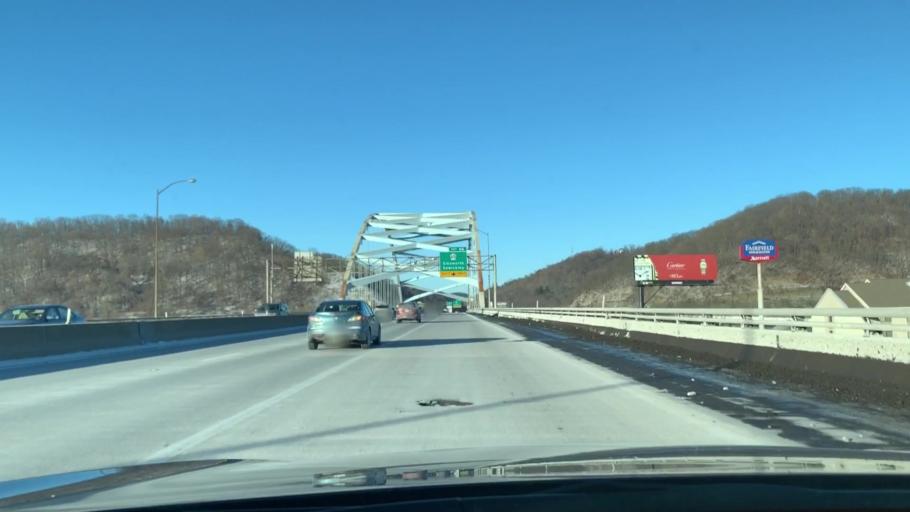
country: US
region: Pennsylvania
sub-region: Allegheny County
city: Coraopolis
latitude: 40.5136
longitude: -80.1339
